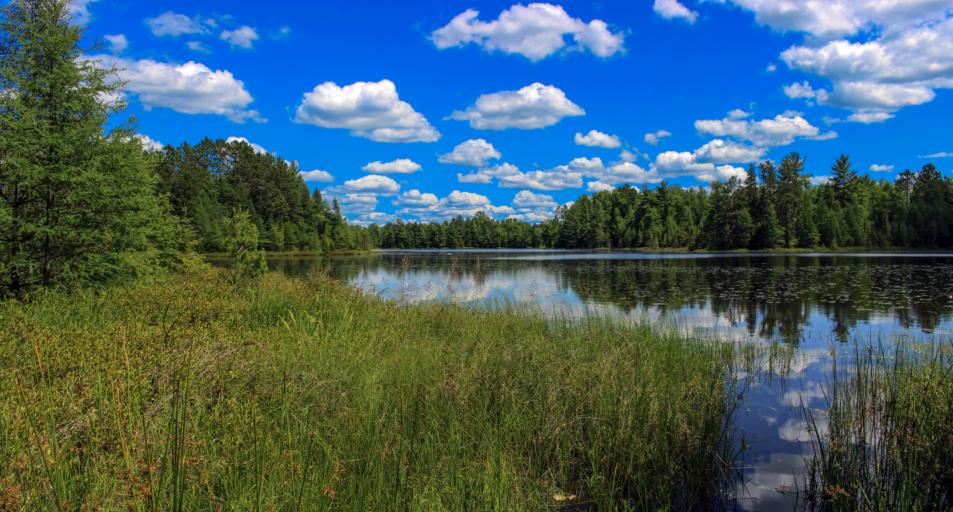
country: US
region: Wisconsin
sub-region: Oneida County
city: Rhinelander
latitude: 45.7748
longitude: -89.4816
